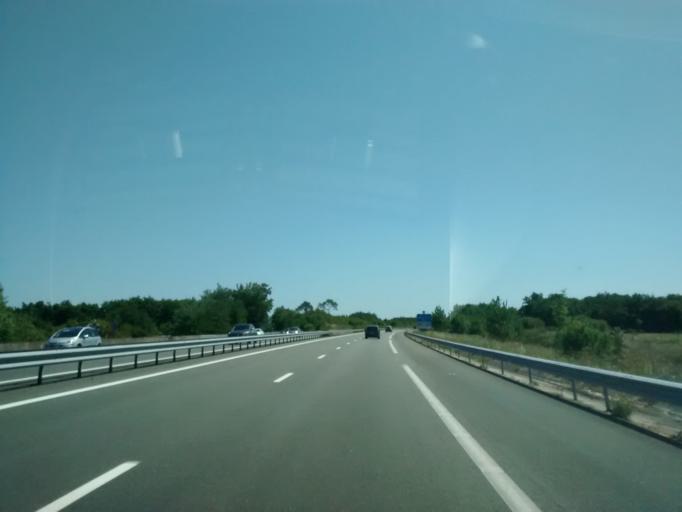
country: FR
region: Aquitaine
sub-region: Departement de la Gironde
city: Saint-Seurin-sur-l'Isle
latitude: 45.0028
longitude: 0.0286
